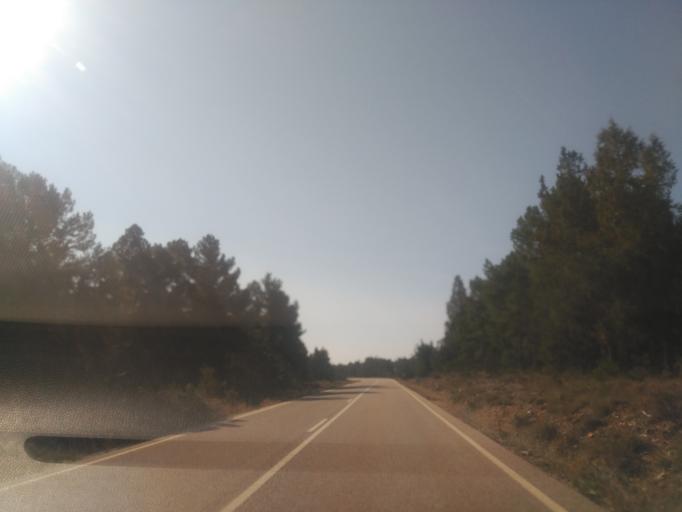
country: ES
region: Castille and Leon
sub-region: Provincia de Soria
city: Ucero
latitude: 41.7409
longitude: -3.0448
